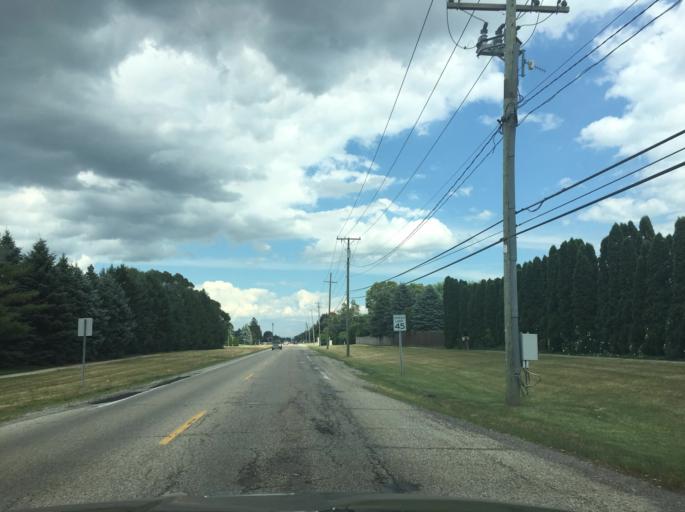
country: US
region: Michigan
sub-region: Macomb County
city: Utica
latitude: 42.6410
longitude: -83.0006
